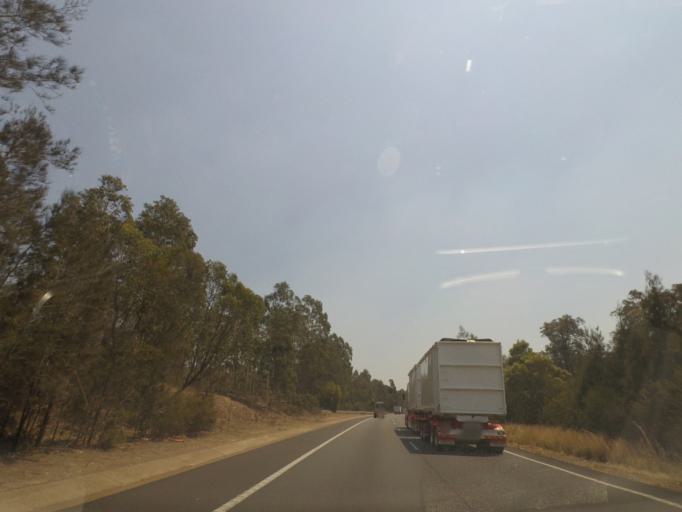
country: AU
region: New South Wales
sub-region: Newcastle
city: Beresfield
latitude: -32.8292
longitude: 151.6332
